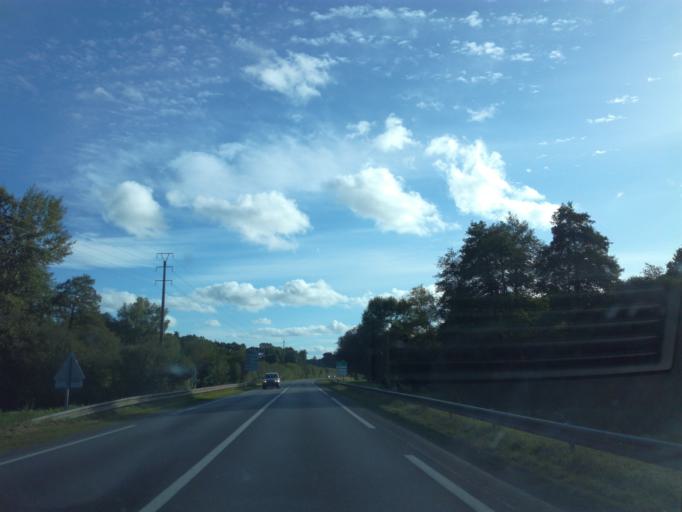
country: FR
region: Brittany
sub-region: Departement du Morbihan
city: Saint-Thuriau
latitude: 48.0512
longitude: -2.9446
